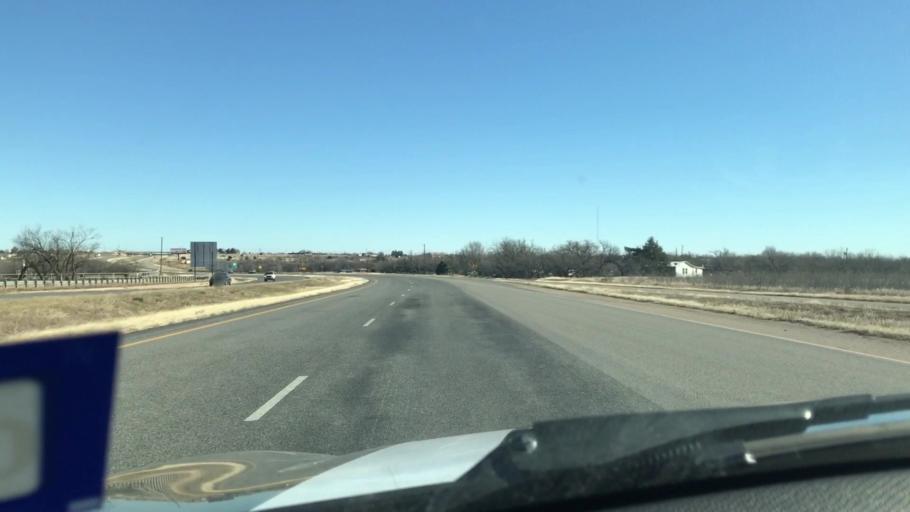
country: US
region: Texas
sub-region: Scurry County
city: Snyder
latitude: 32.7362
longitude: -100.9146
